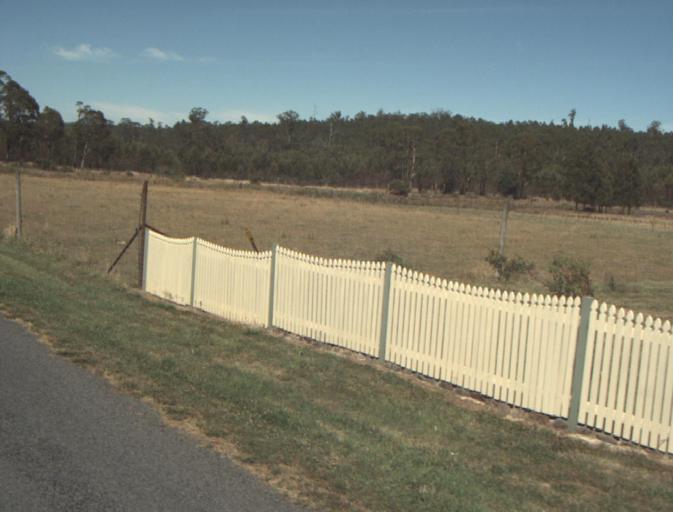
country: AU
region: Tasmania
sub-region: Launceston
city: Newstead
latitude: -41.3774
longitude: 147.2965
